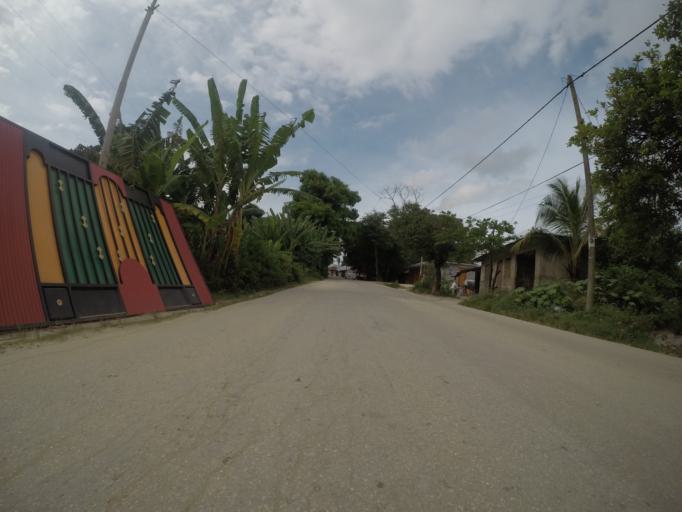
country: TZ
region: Pemba South
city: Chake Chake
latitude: -5.2426
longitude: 39.7823
